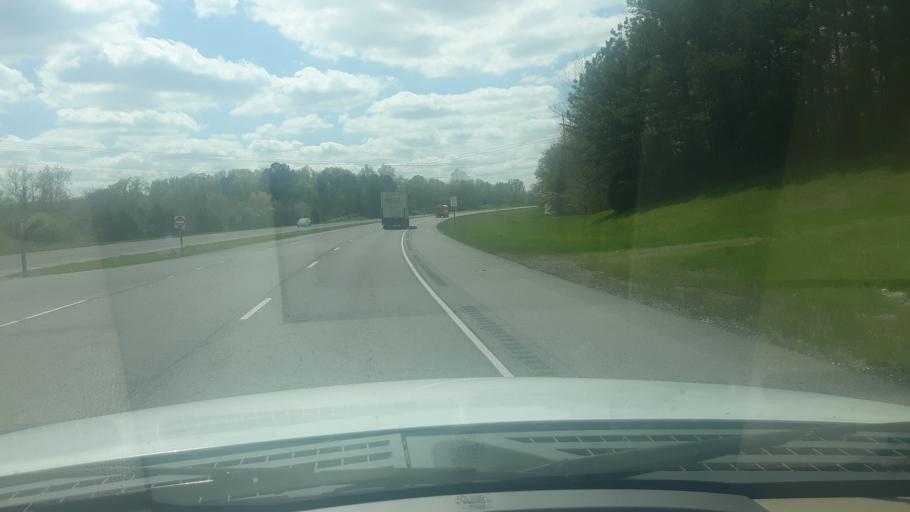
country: US
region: Illinois
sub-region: Williamson County
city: Marion
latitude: 37.7316
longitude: -88.8200
